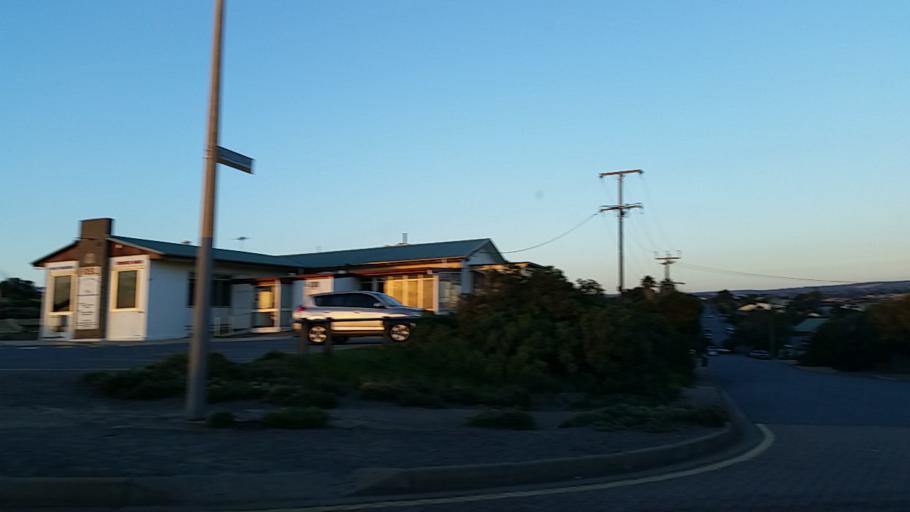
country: AU
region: South Australia
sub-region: Adelaide
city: Port Noarlunga
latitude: -35.1469
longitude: 138.4672
